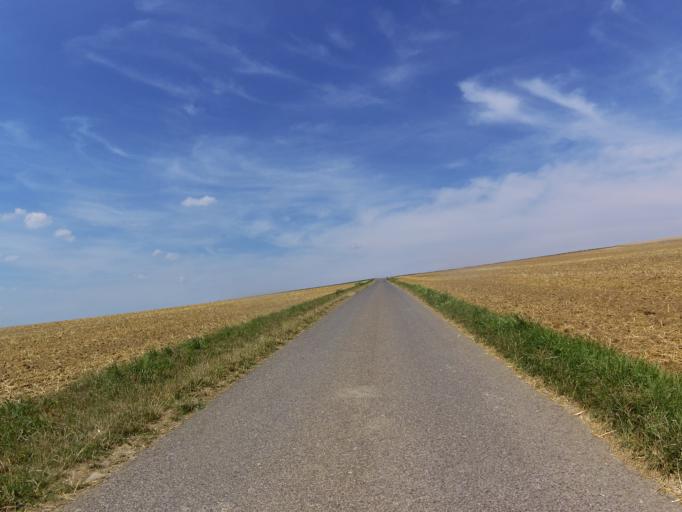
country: DE
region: Bavaria
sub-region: Regierungsbezirk Unterfranken
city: Estenfeld
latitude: 49.8124
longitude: 10.0112
